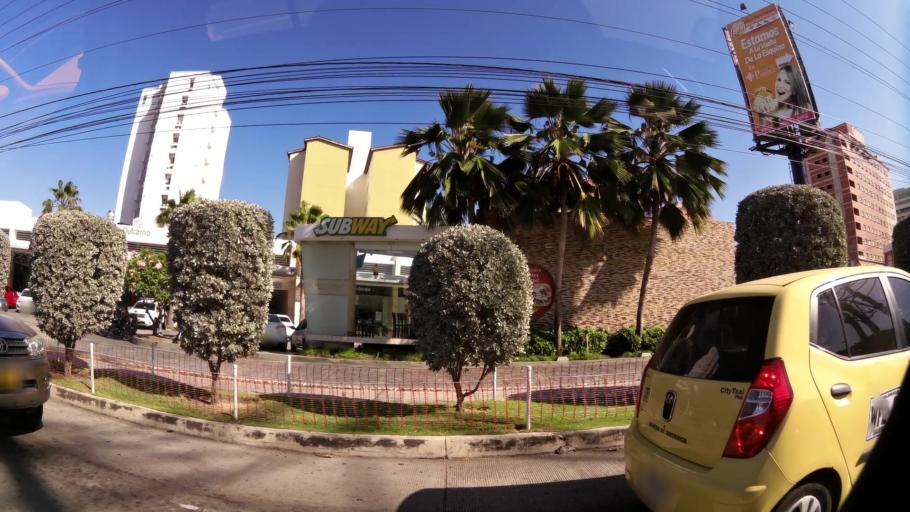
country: CO
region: Atlantico
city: Barranquilla
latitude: 11.0141
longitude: -74.8264
